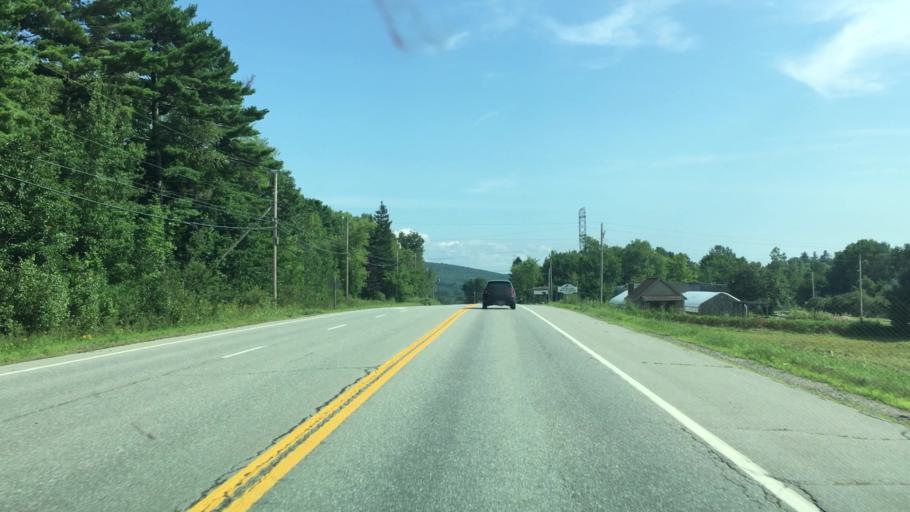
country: US
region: Maine
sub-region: Waldo County
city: Winterport
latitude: 44.6774
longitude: -68.8412
